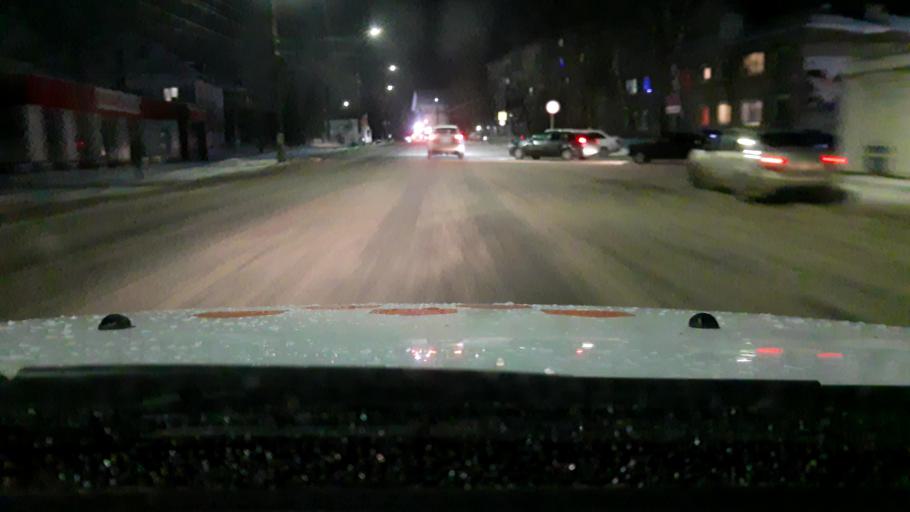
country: RU
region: Nizjnij Novgorod
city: Gorodets
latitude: 56.6660
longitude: 43.4676
